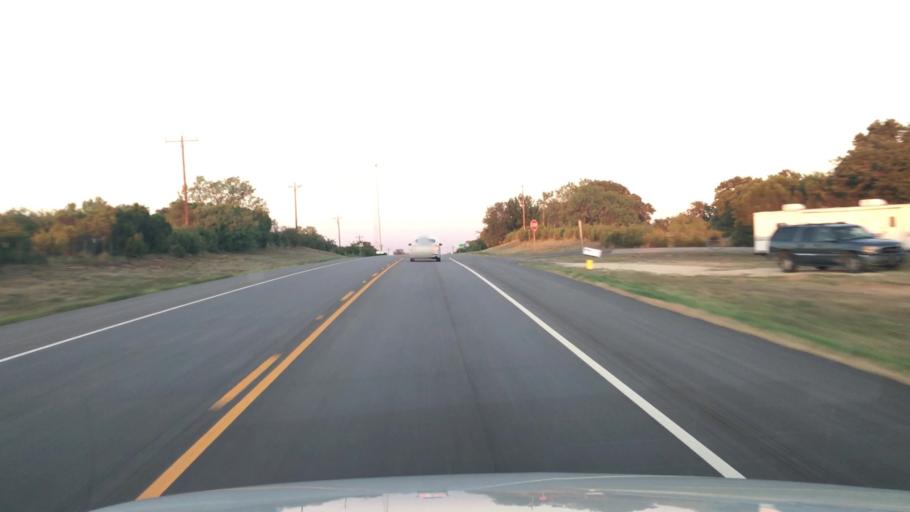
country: US
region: Texas
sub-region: Somervell County
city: Glen Rose
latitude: 32.1921
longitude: -97.8416
